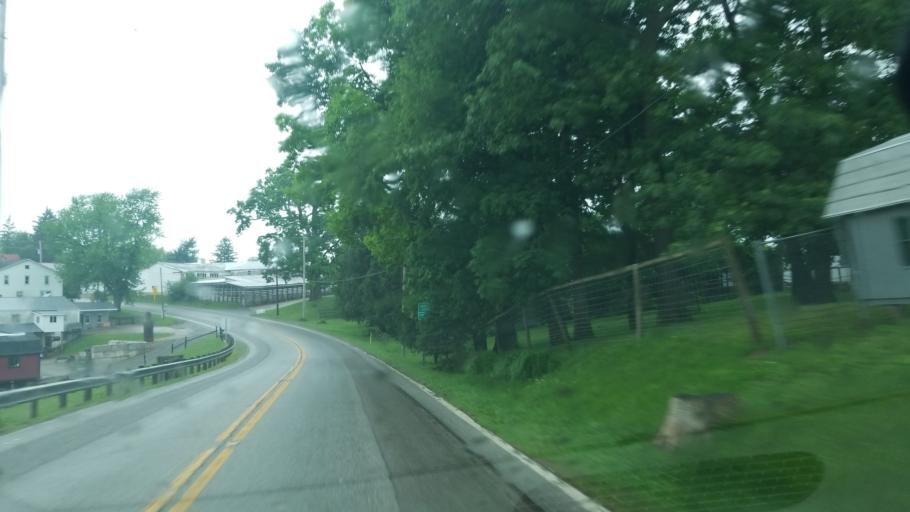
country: US
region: Ohio
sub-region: Tuscarawas County
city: Sugarcreek
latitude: 40.4855
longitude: -81.7268
